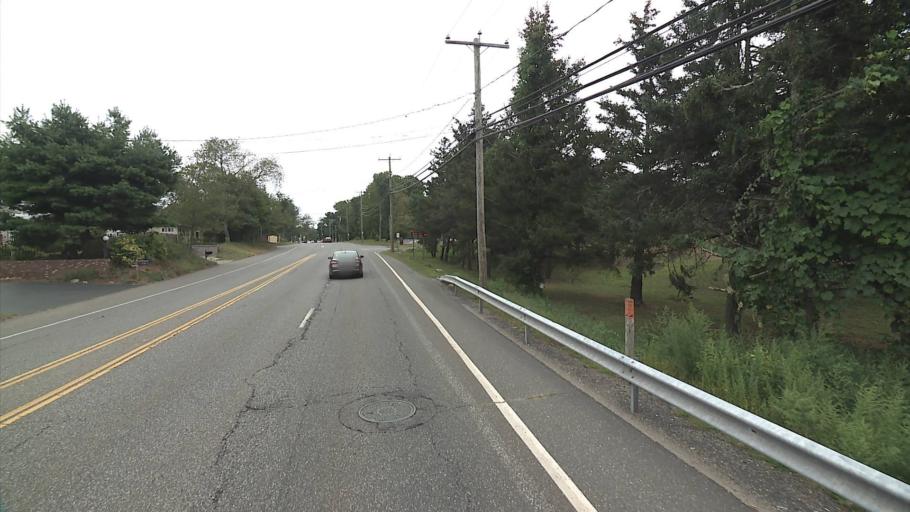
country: US
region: Connecticut
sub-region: New London County
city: Niantic
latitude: 41.3170
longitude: -72.2422
